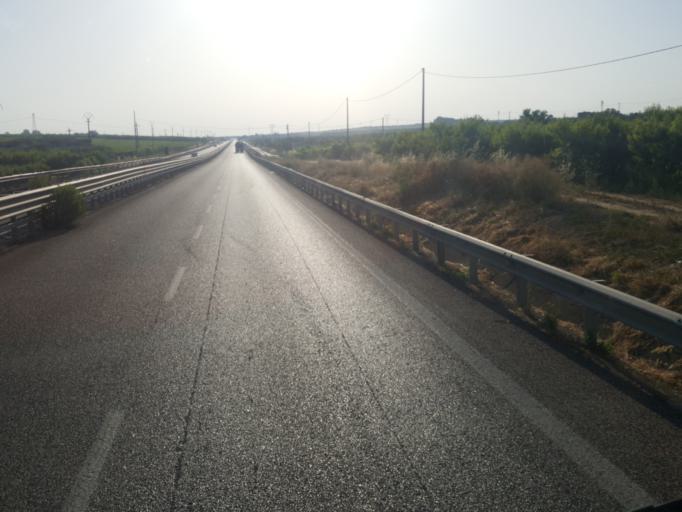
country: IT
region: Apulia
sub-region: Provincia di Foggia
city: Cerignola
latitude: 41.2789
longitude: 15.9849
